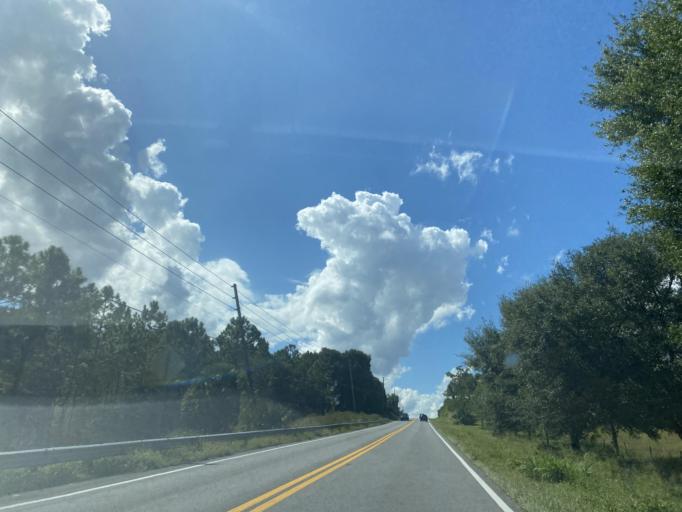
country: US
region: Florida
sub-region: Lake County
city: Lady Lake
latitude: 28.9819
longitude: -81.9112
